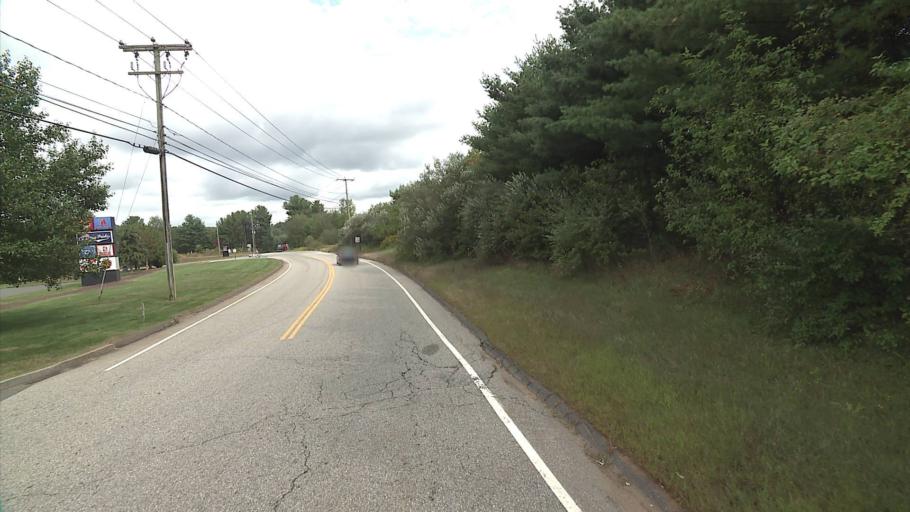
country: US
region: Connecticut
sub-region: Tolland County
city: Stafford Springs
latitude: 41.9177
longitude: -72.2604
